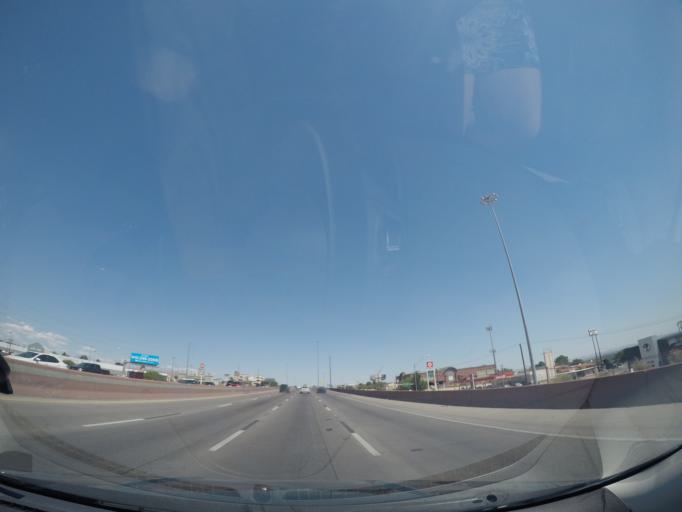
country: US
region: Texas
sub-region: El Paso County
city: Fort Bliss
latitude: 31.7594
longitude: -106.3564
